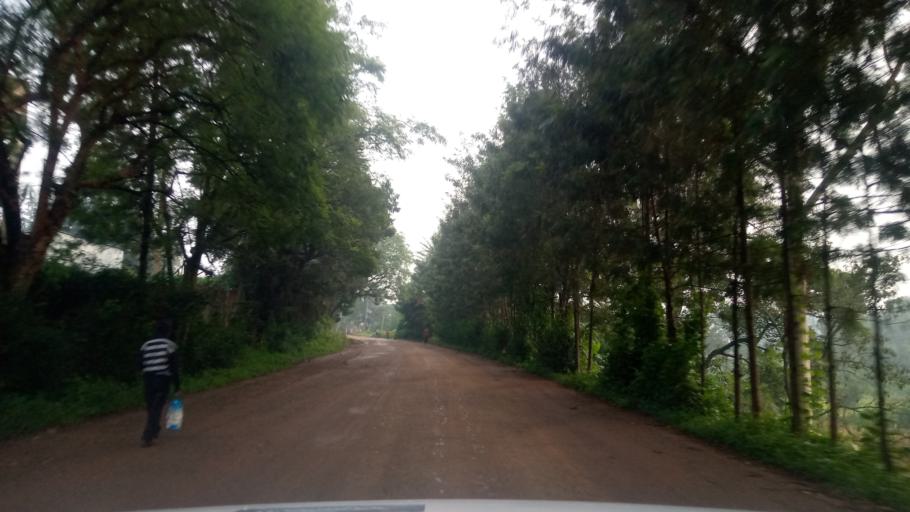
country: ET
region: Oromiya
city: Jima
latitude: 7.6859
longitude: 36.8319
